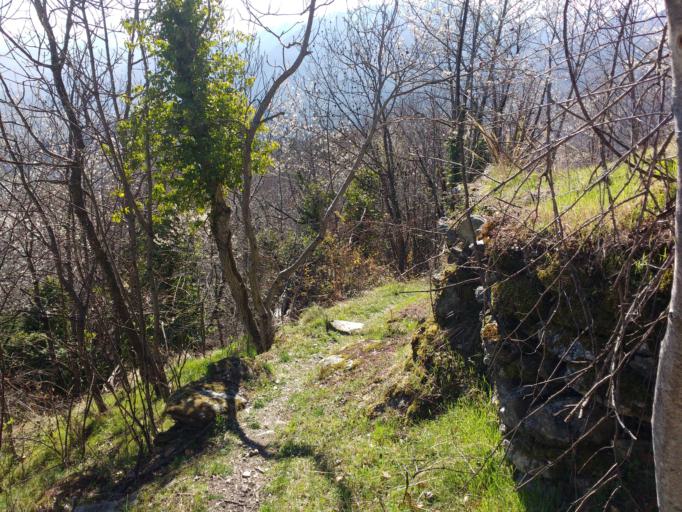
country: IT
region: Piedmont
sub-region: Provincia di Torino
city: Giaglione
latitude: 45.1457
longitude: 7.0101
